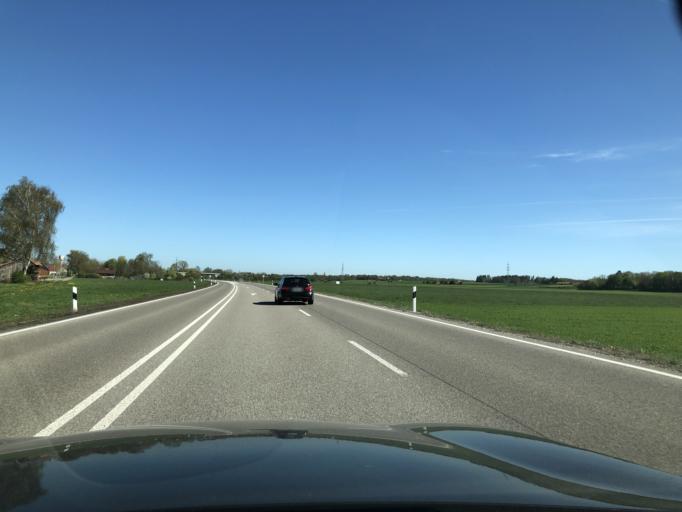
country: DE
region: Bavaria
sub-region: Swabia
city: Jengen
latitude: 48.0121
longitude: 10.7233
